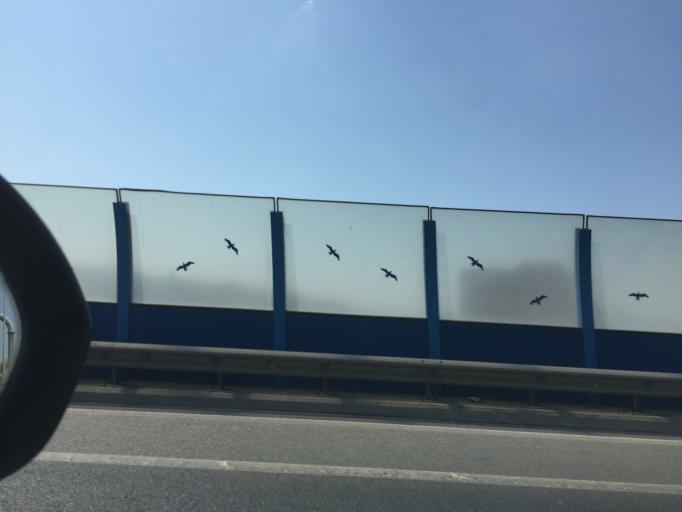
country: TR
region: Izmir
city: Karsiyaka
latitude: 38.4856
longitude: 27.1363
